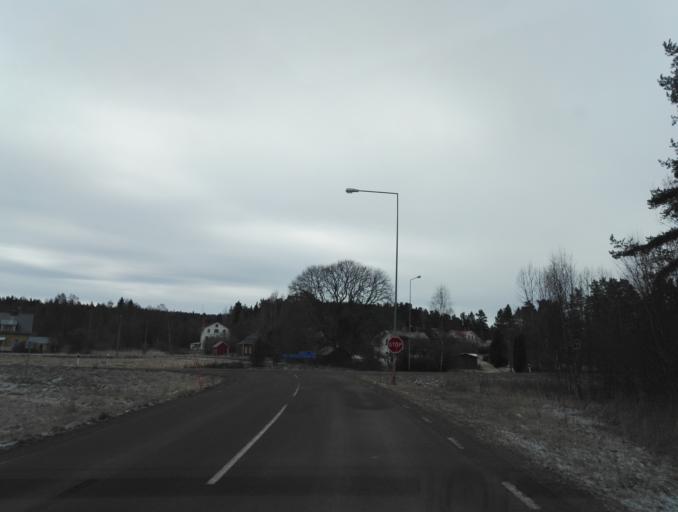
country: SE
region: Kalmar
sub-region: Hultsfreds Kommun
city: Virserum
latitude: 57.3443
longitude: 15.6061
